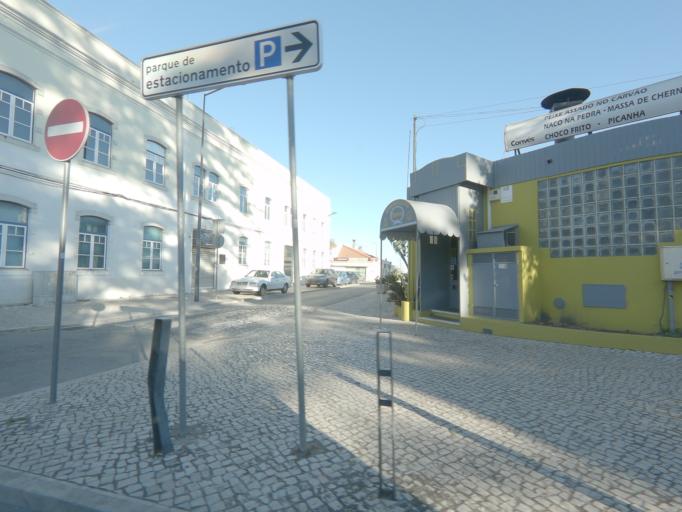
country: PT
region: Setubal
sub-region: Setubal
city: Setubal
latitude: 38.5201
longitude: -8.9026
